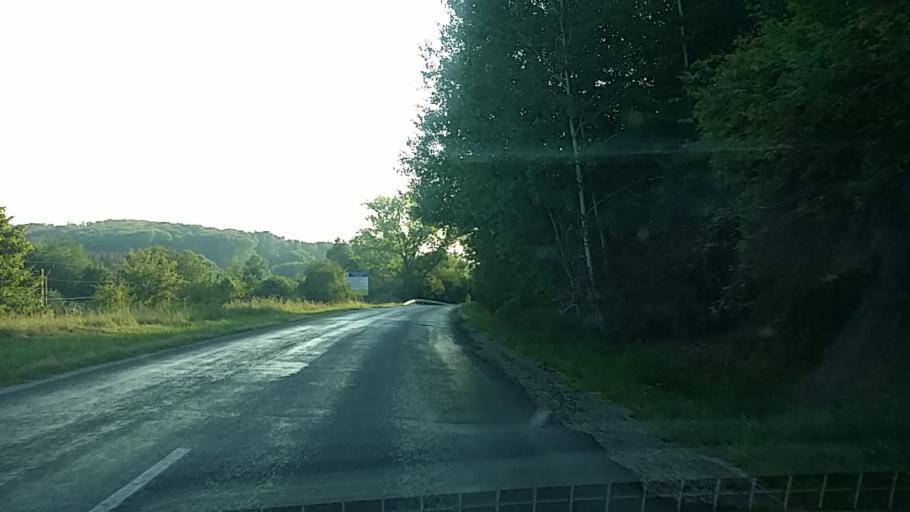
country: HU
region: Baranya
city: Buekkoesd
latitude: 46.1545
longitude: 18.0810
